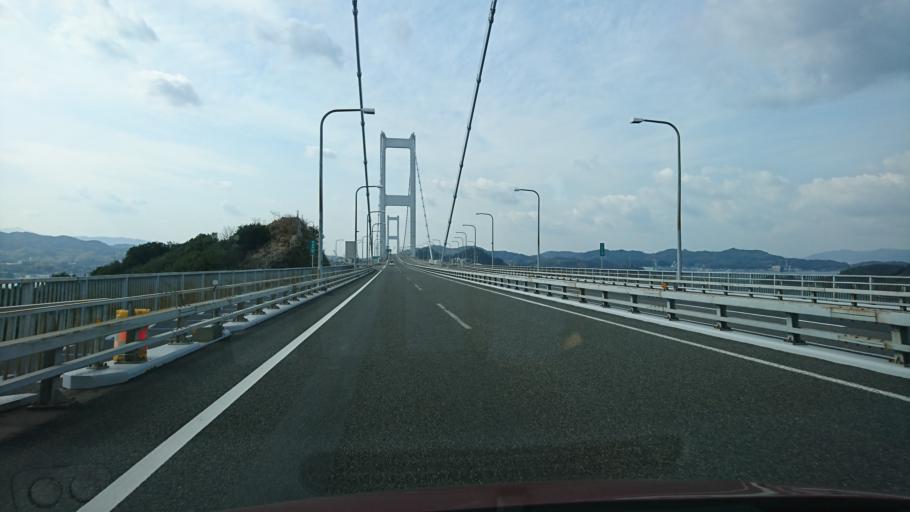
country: JP
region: Hiroshima
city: Takehara
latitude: 34.1191
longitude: 132.9948
